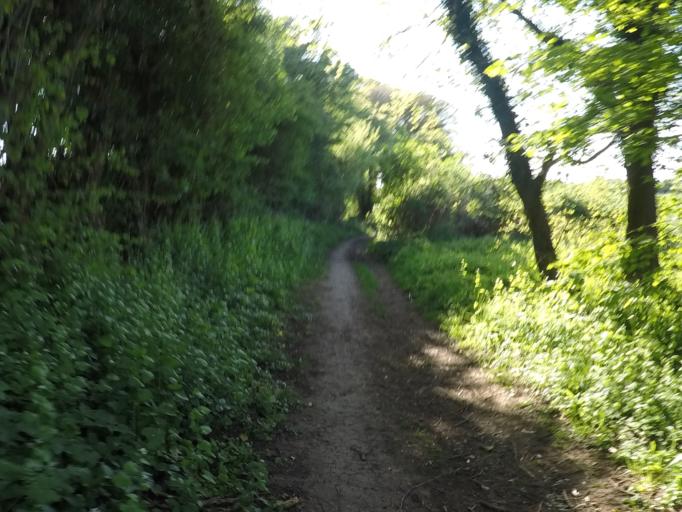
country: GB
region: England
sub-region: Oxfordshire
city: Charlbury
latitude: 51.8752
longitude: -1.4598
